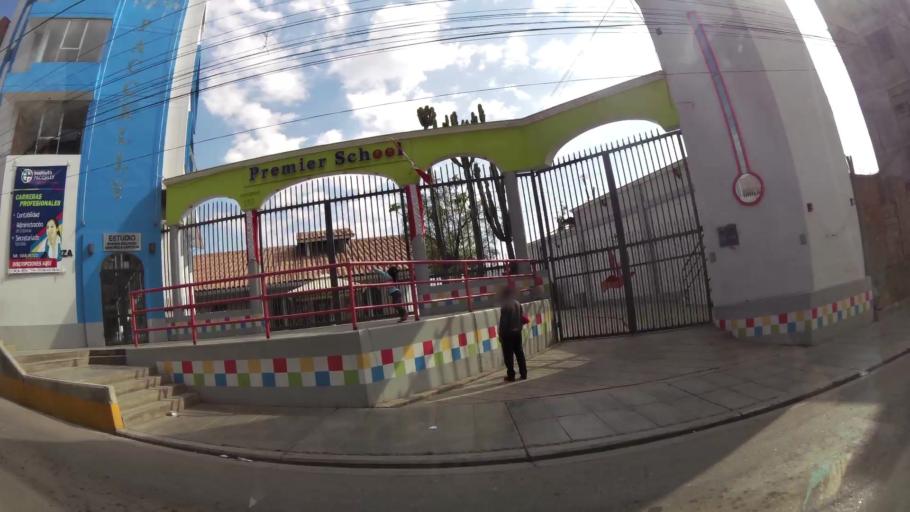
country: PE
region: Junin
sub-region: Provincia de Huancayo
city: Huancayo
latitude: -12.0637
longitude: -75.2100
